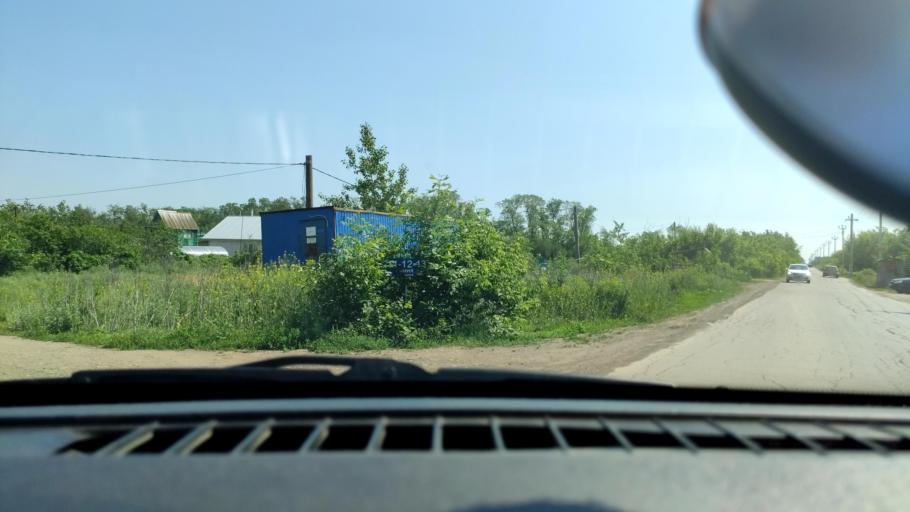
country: RU
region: Samara
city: Novokuybyshevsk
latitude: 53.0725
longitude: 50.0665
